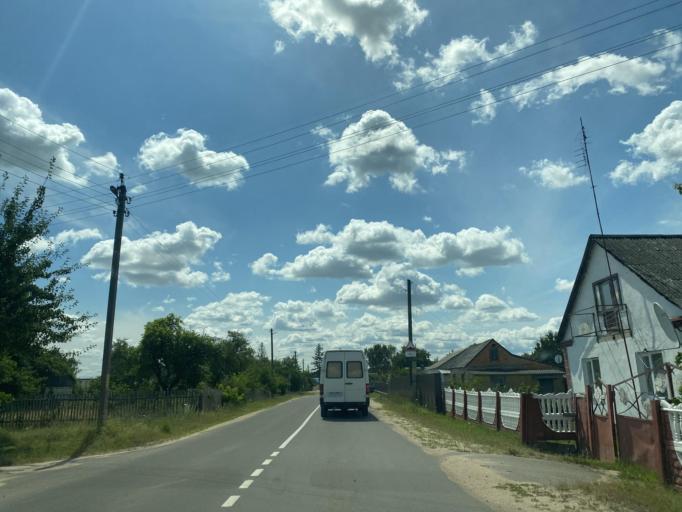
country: BY
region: Brest
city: Ivanava
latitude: 52.1431
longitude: 25.5468
